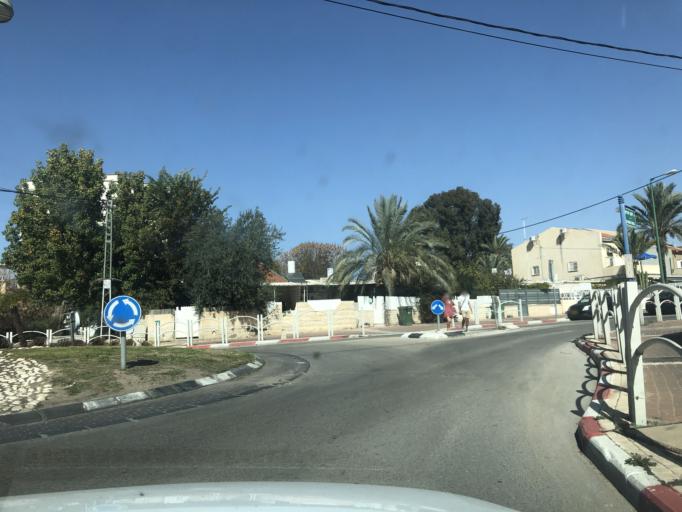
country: IL
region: Southern District
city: Beersheba
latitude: 31.2618
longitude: 34.7952
